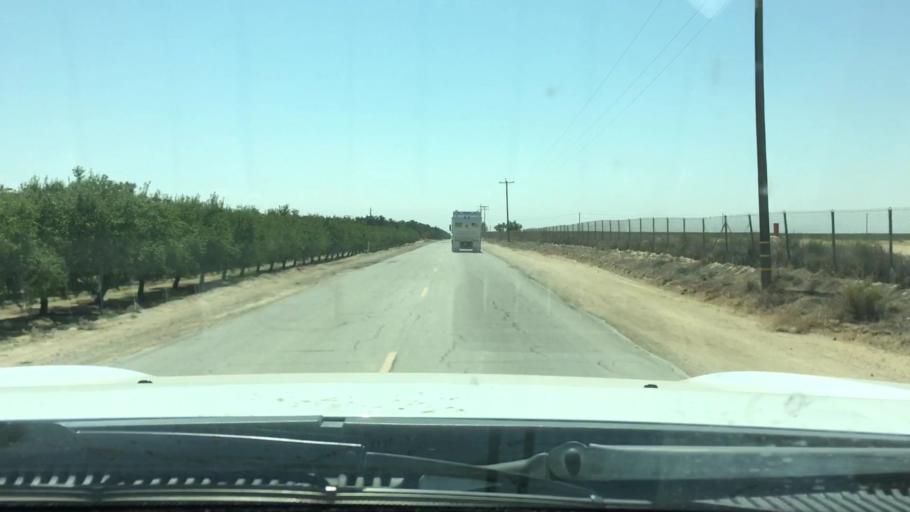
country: US
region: California
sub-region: Kern County
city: Wasco
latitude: 35.5102
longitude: -119.4033
